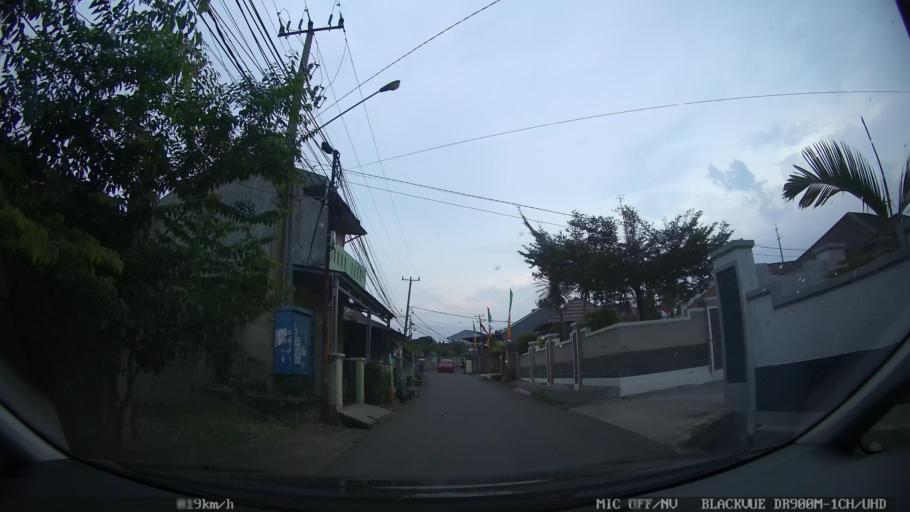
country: ID
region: Lampung
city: Kedaton
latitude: -5.3990
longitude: 105.2712
